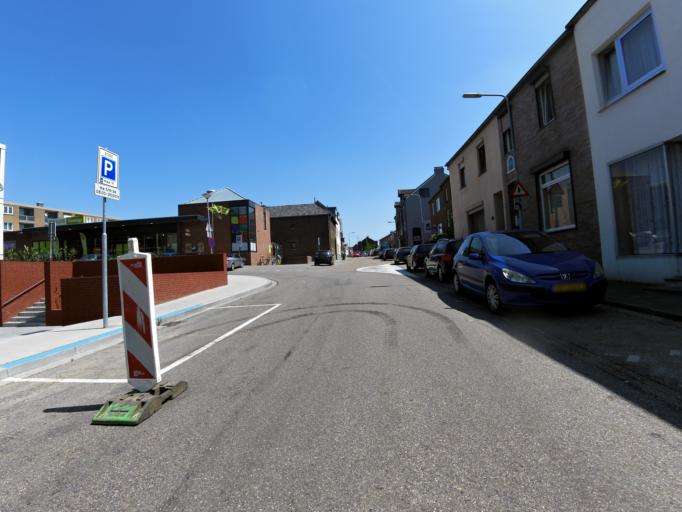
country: NL
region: Limburg
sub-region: Gemeente Simpelveld
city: Simpelveld
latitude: 50.8172
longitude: 6.0098
